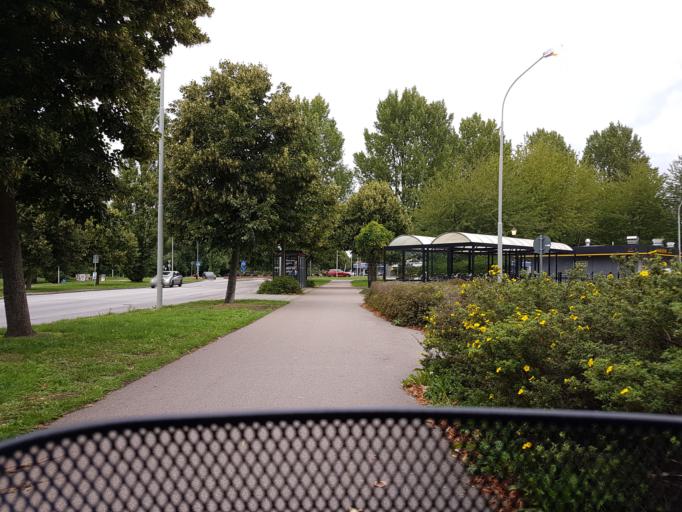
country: SE
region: Skane
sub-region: Landskrona
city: Landskrona
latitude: 55.8850
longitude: 12.8316
